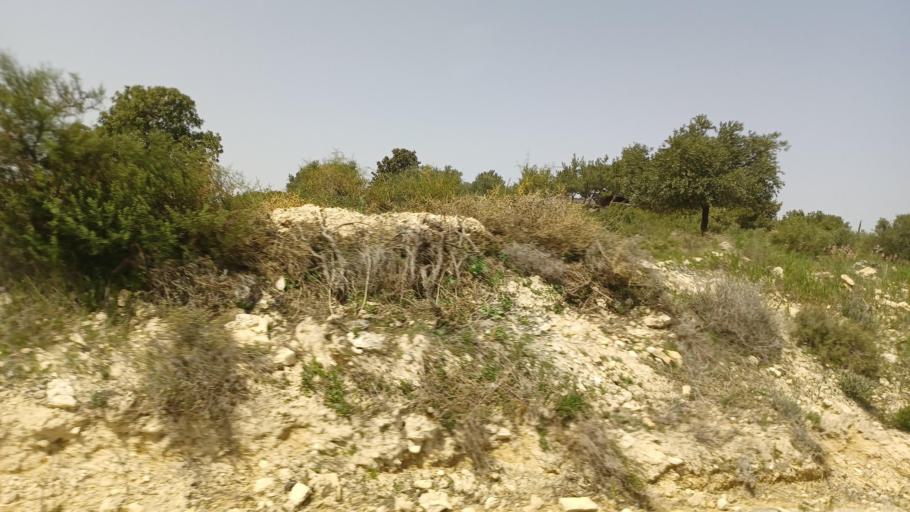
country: CY
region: Limassol
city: Pachna
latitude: 34.7498
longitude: 32.7451
